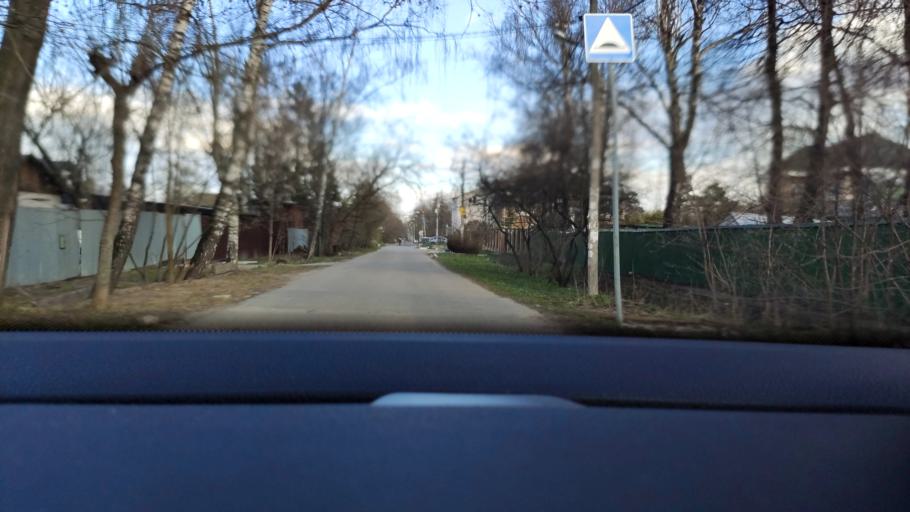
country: RU
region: Moskovskaya
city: Reutov
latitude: 55.7724
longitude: 37.8939
